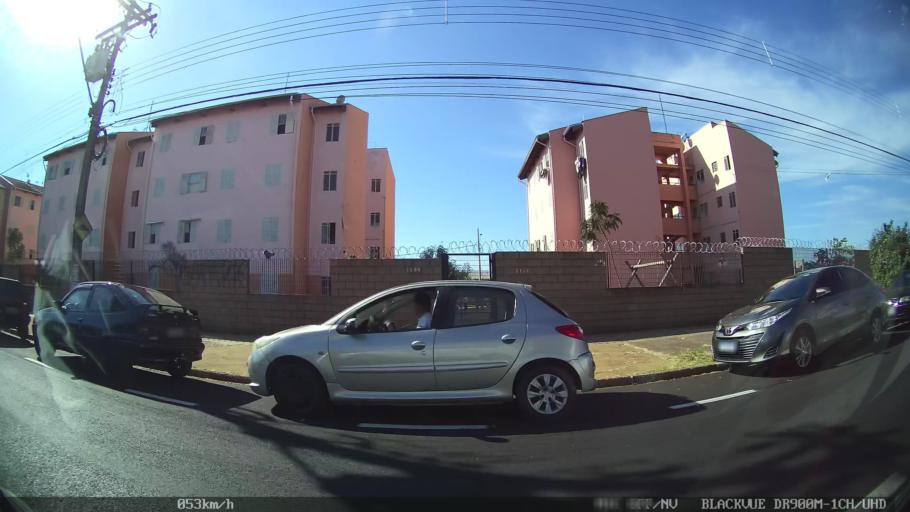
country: BR
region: Sao Paulo
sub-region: Franca
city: Franca
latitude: -20.4982
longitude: -47.4177
